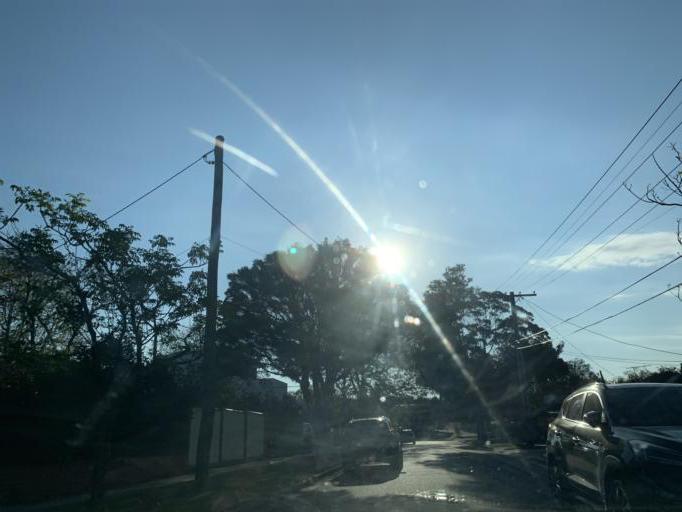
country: AU
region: Victoria
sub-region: Kingston
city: Parkdale
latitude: -37.9864
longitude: 145.0817
